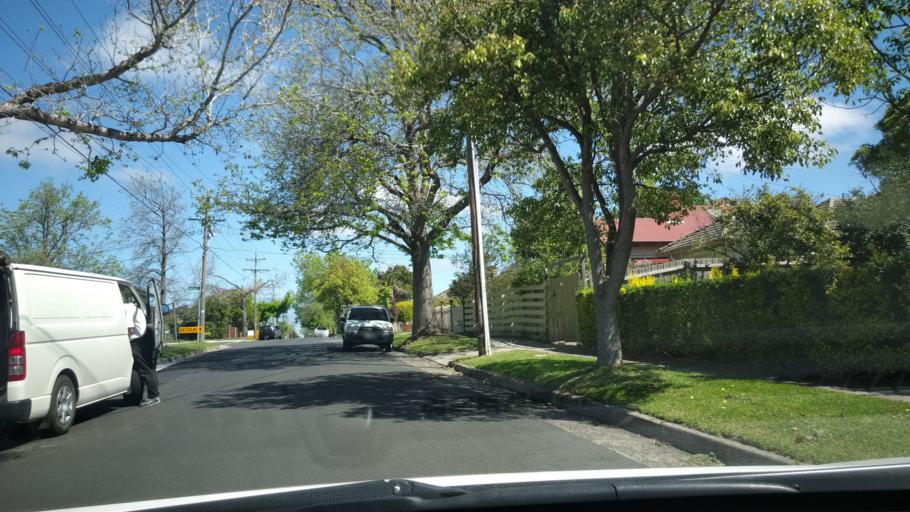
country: AU
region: Victoria
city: Murrumbeena
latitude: -37.9047
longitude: 145.0691
